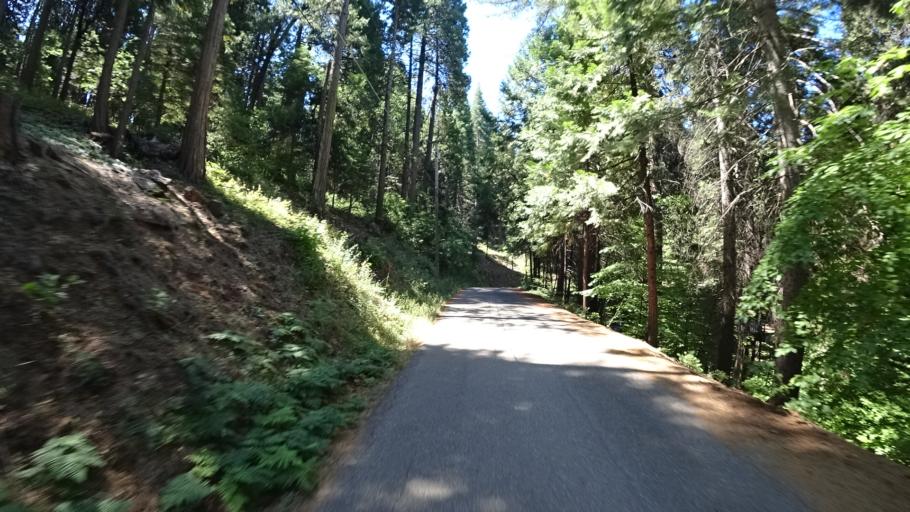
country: US
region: California
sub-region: Calaveras County
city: Arnold
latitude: 38.2287
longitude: -120.3759
